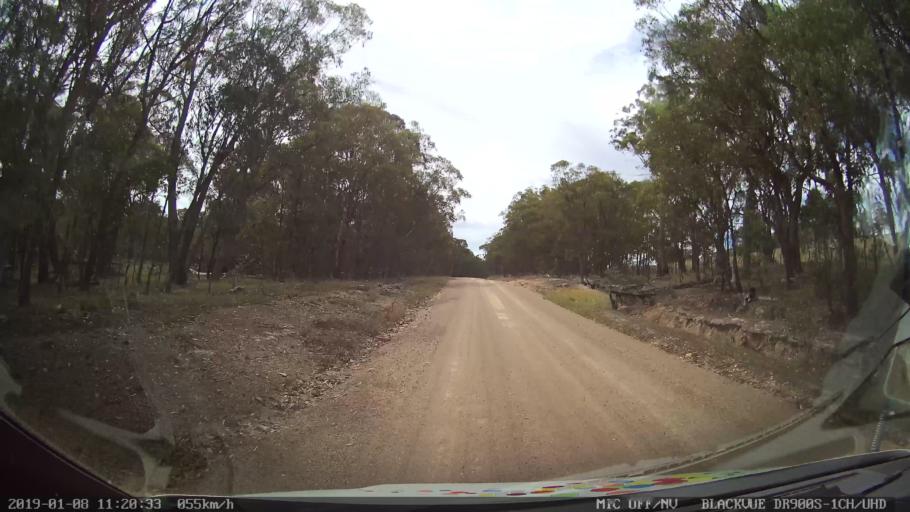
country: AU
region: New South Wales
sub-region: Guyra
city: Guyra
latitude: -30.2313
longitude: 151.5621
